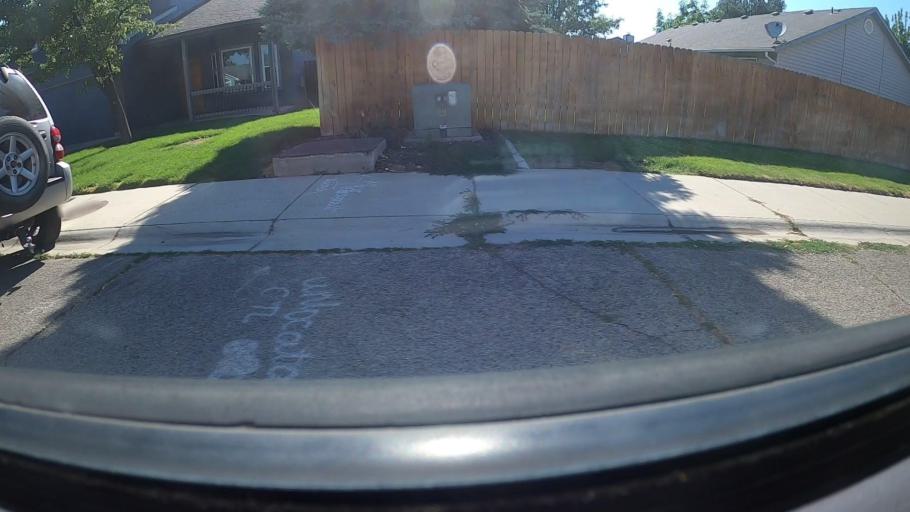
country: US
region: Idaho
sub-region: Ada County
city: Meridian
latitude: 43.6250
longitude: -116.3650
